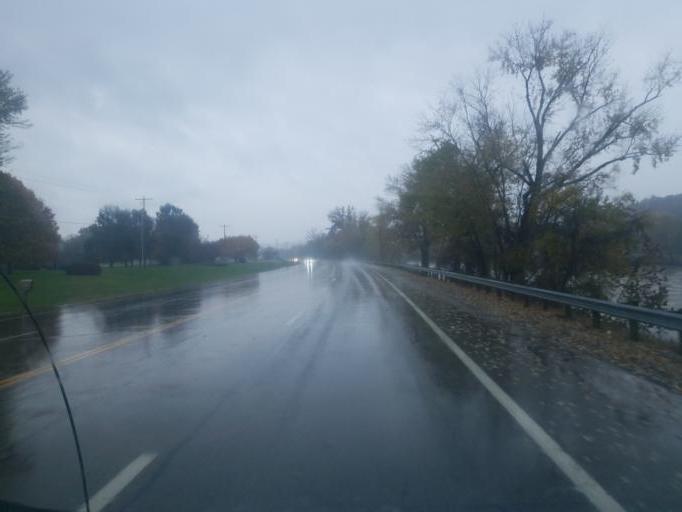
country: US
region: Ohio
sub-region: Muskingum County
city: South Zanesville
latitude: 39.8862
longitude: -81.9885
